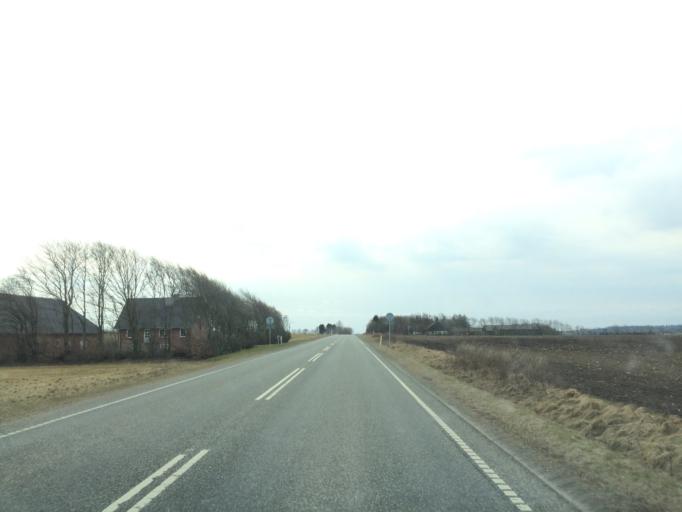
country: DK
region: Central Jutland
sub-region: Ringkobing-Skjern Kommune
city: Videbaek
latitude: 56.0830
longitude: 8.5070
